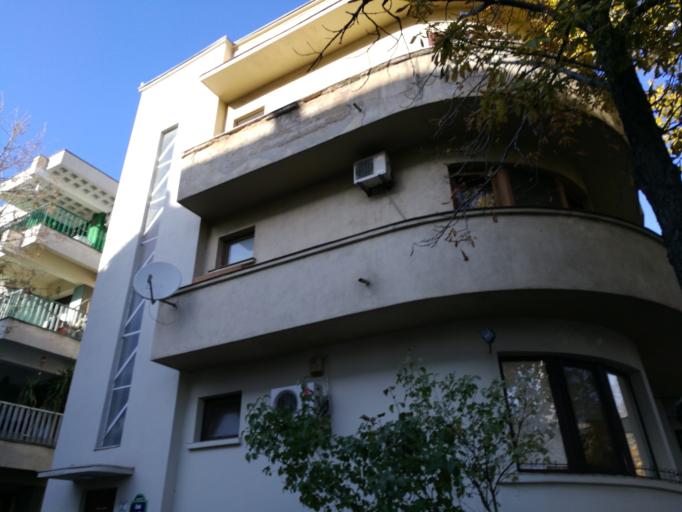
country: RO
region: Bucuresti
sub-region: Municipiul Bucuresti
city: Bucharest
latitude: 44.4638
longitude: 26.0953
